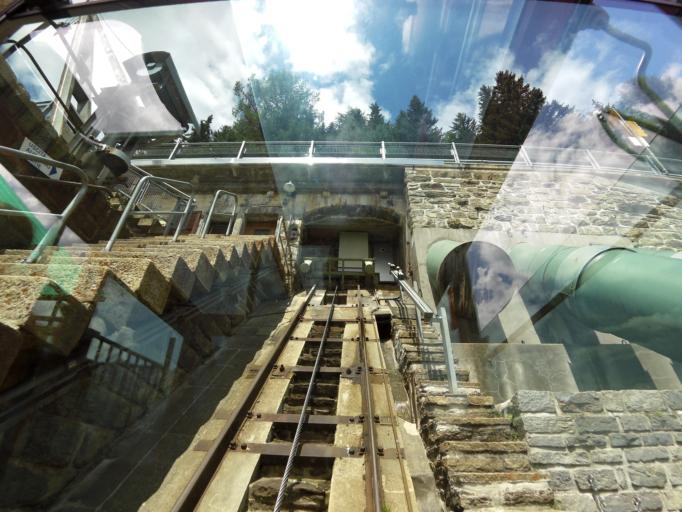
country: CH
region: Ticino
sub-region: Leventina District
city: Airolo
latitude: 46.5284
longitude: 8.6715
